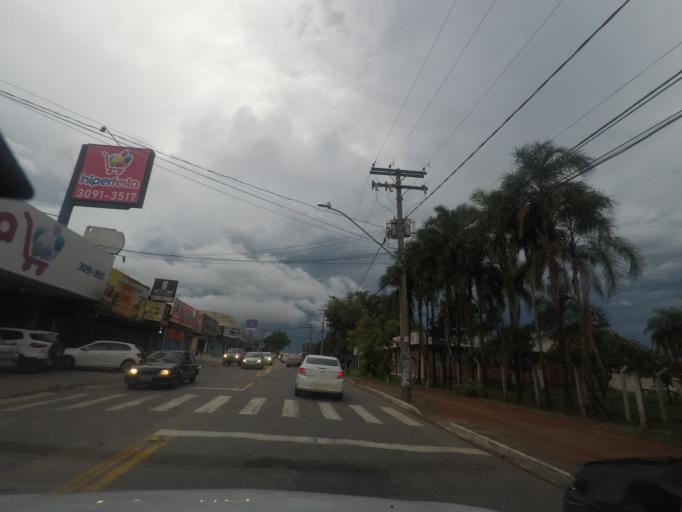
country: BR
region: Goias
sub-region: Goiania
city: Goiania
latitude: -16.7291
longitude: -49.2393
